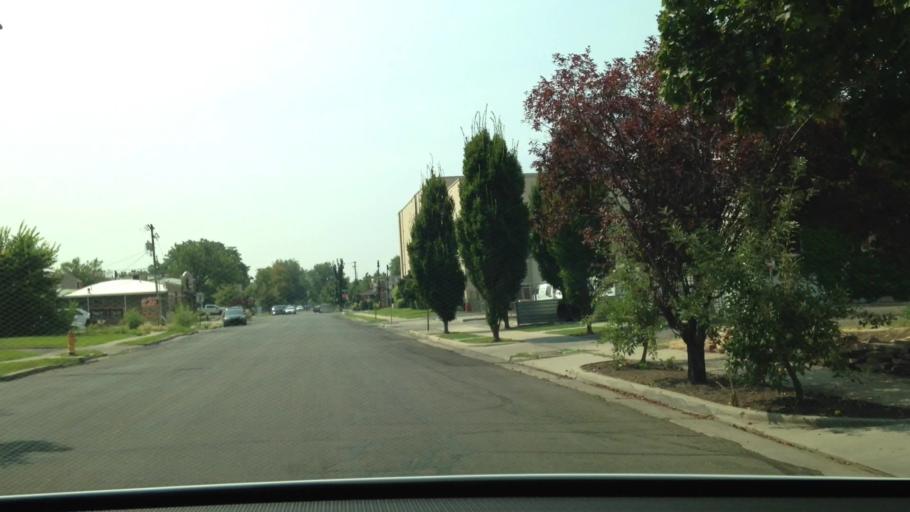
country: US
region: Utah
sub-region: Salt Lake County
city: South Salt Lake
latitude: 40.7268
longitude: -111.8682
